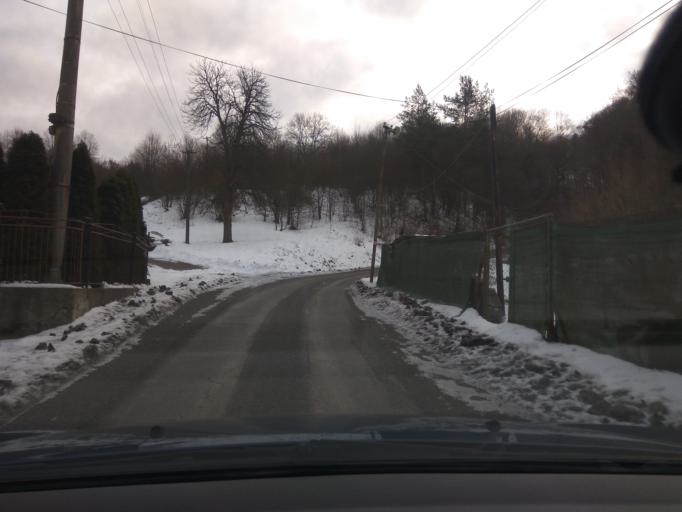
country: SK
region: Banskobystricky
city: Zarnovica
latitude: 48.4822
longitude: 18.7474
